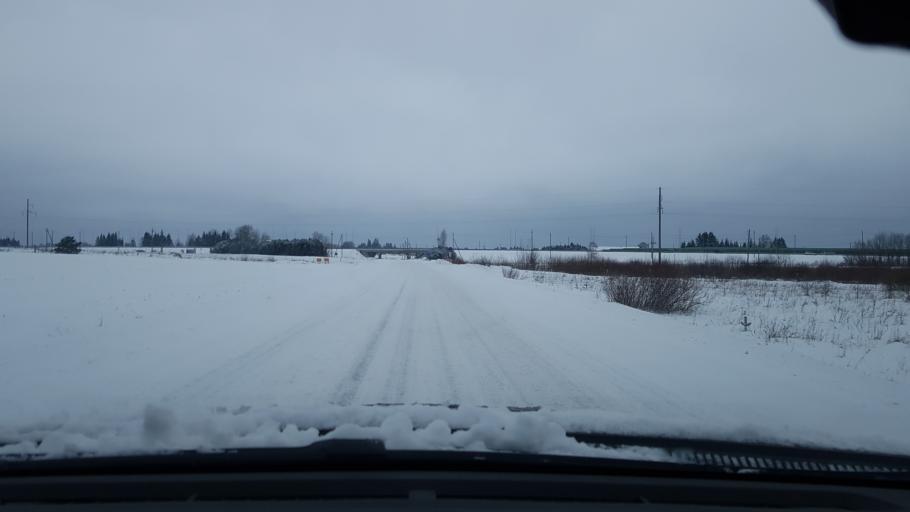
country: EE
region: Harju
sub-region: Kuusalu vald
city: Kuusalu
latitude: 59.4422
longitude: 25.3803
